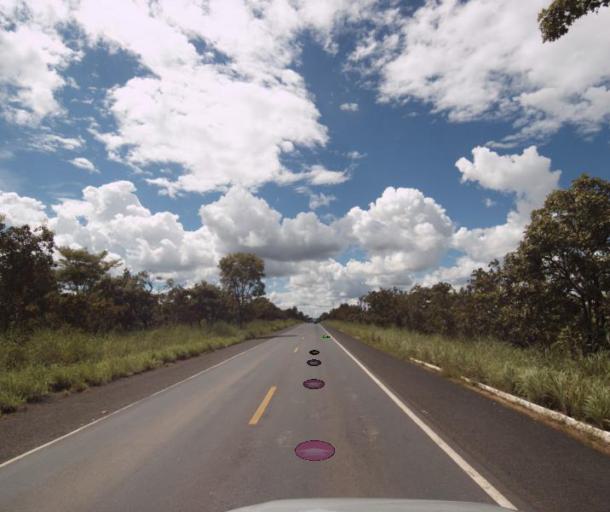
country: BR
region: Goias
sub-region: Porangatu
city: Porangatu
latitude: -13.8362
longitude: -49.0448
